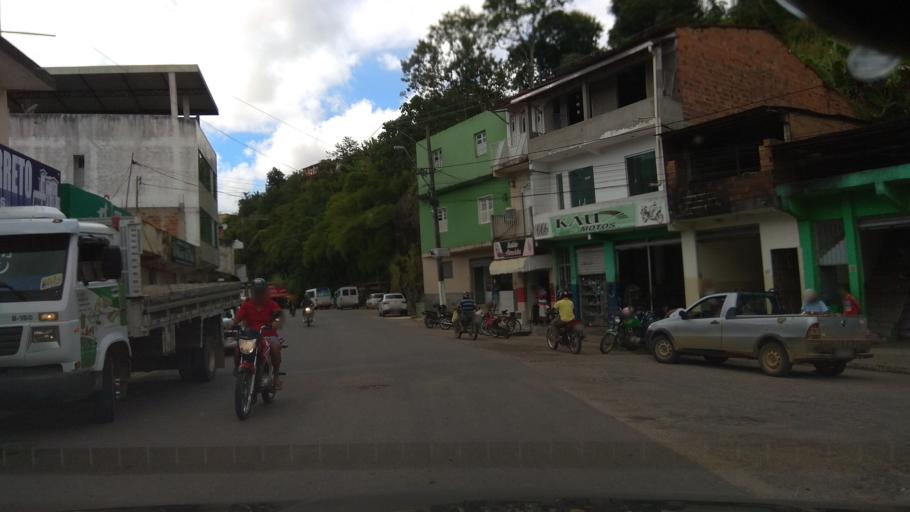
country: BR
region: Bahia
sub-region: Mutuipe
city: Mutuipe
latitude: -13.2274
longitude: -39.5021
